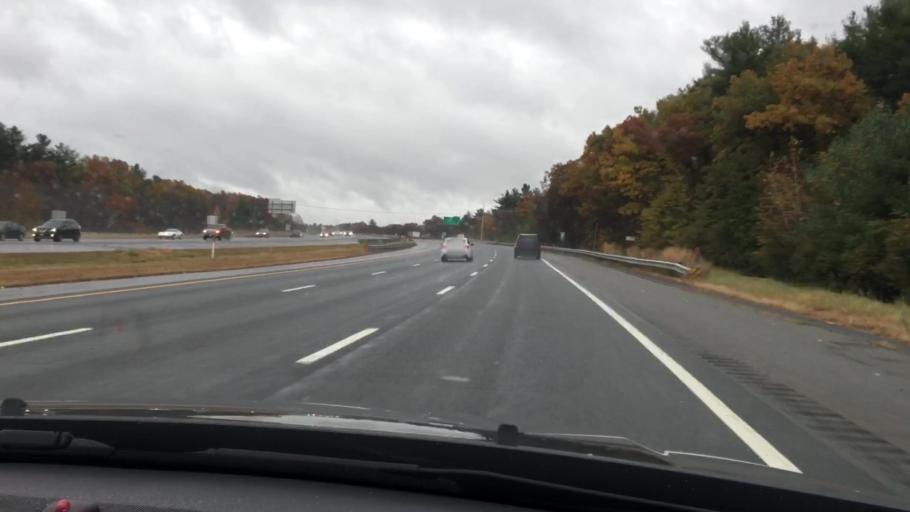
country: US
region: Massachusetts
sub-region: Middlesex County
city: Tyngsboro
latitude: 42.6337
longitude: -71.4078
